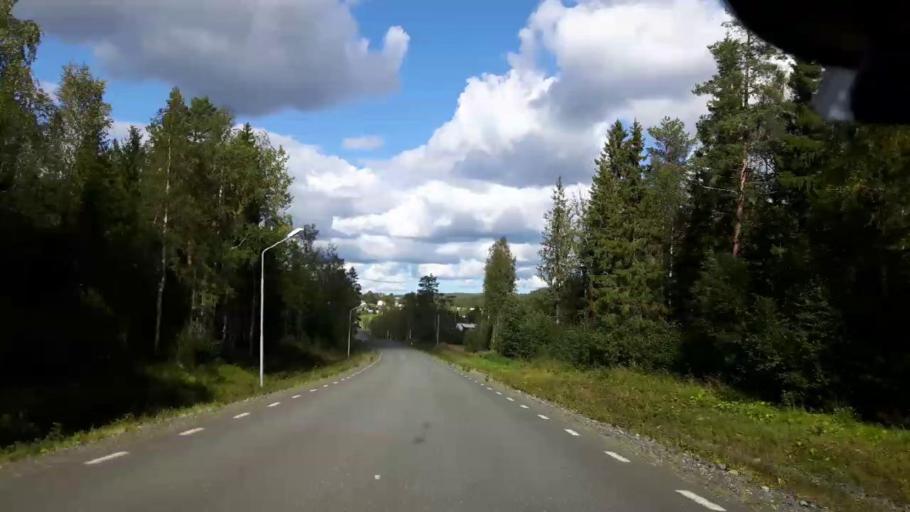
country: SE
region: Jaemtland
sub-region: Stroemsunds Kommun
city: Stroemsund
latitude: 63.2898
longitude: 15.5897
